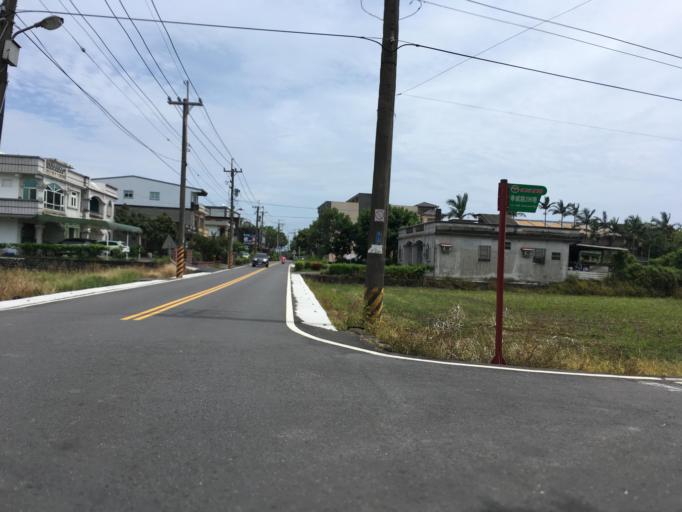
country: TW
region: Taiwan
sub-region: Yilan
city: Yilan
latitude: 24.6950
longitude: 121.8109
